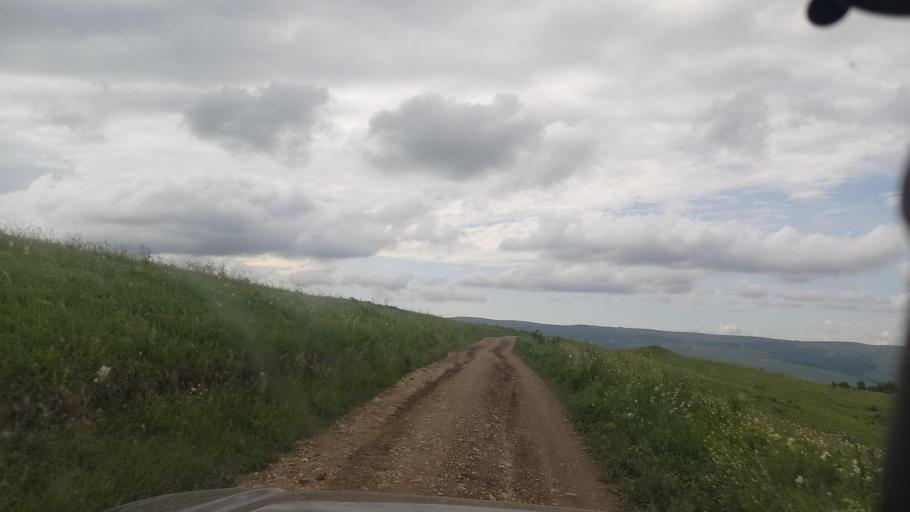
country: RU
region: Krasnodarskiy
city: Peredovaya
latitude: 44.0635
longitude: 41.3609
